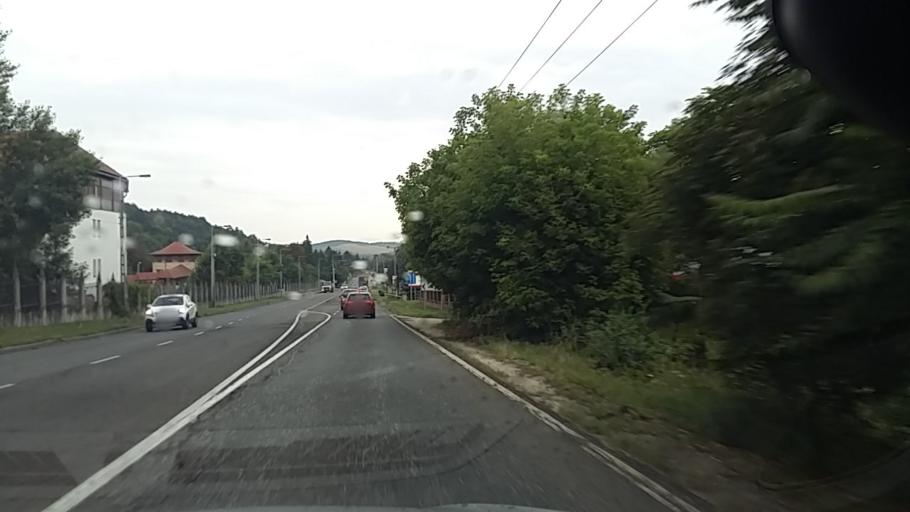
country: HU
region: Pest
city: Piliscsaba
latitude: 47.6308
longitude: 18.8452
